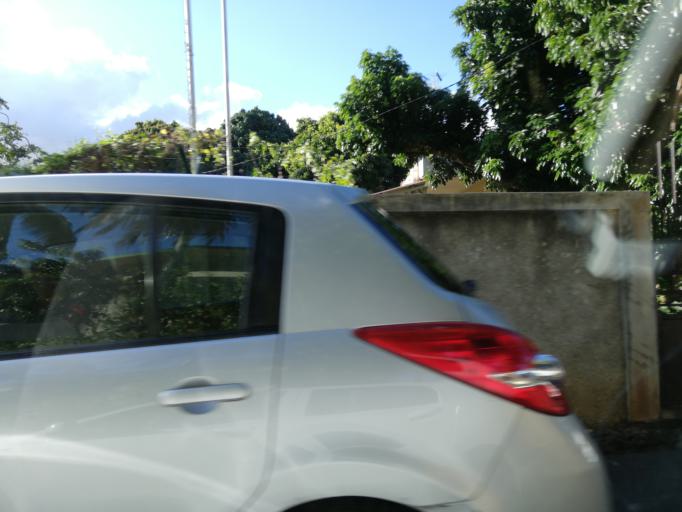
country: MU
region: Moka
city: Moka
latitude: -20.2248
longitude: 57.4689
